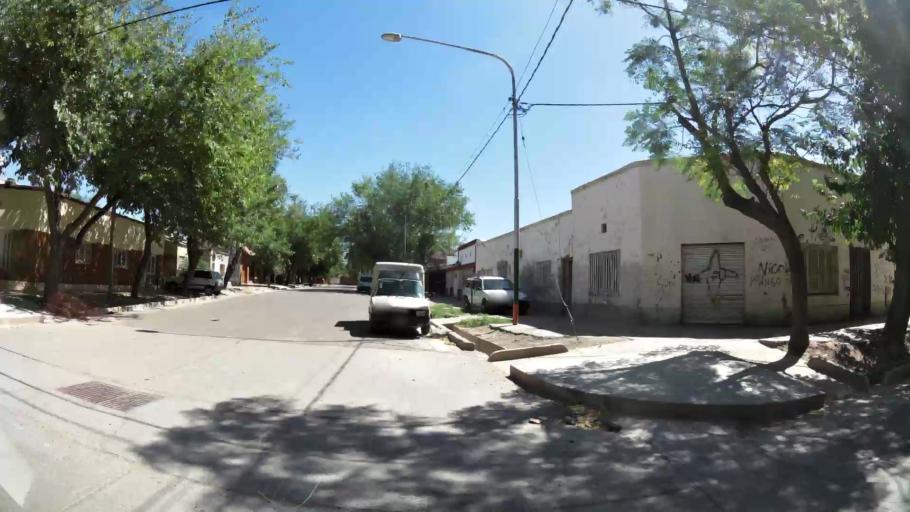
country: AR
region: Mendoza
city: Mendoza
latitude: -32.8774
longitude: -68.8208
